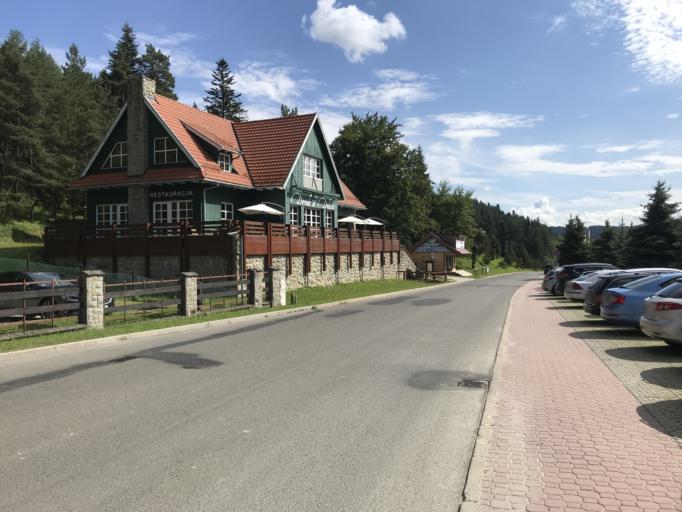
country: PL
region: Lesser Poland Voivodeship
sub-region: Powiat nowosadecki
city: Krynica-Zdroj
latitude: 49.4205
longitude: 20.9260
